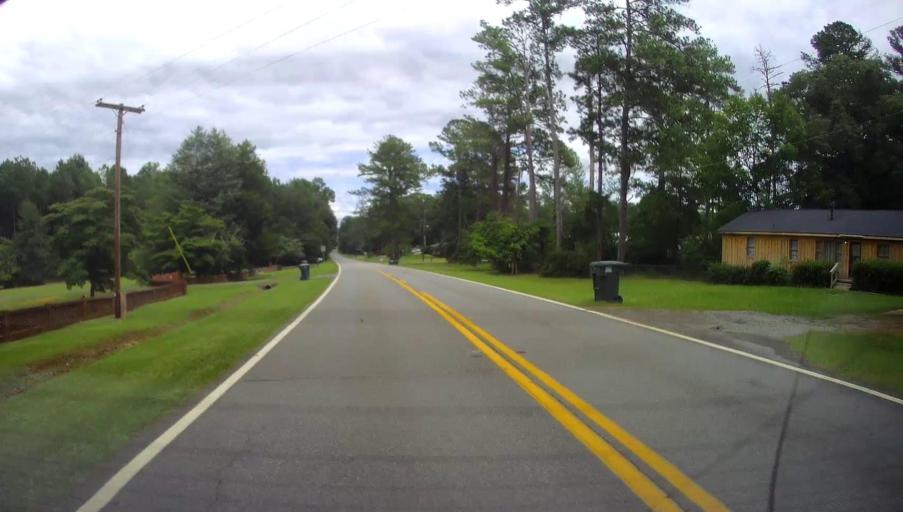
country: US
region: Georgia
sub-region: Twiggs County
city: Jeffersonville
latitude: 32.6791
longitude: -83.3267
